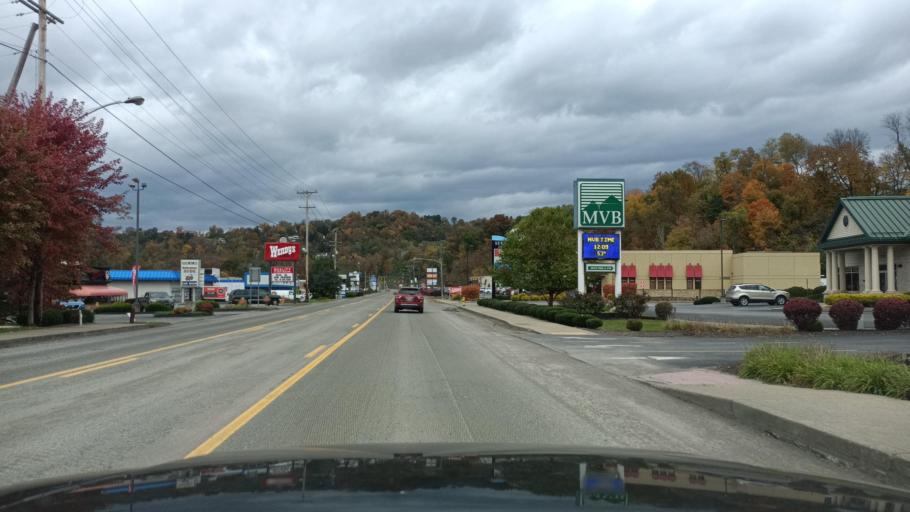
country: US
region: West Virginia
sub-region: Monongalia County
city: Brookhaven
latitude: 39.6269
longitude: -79.9277
